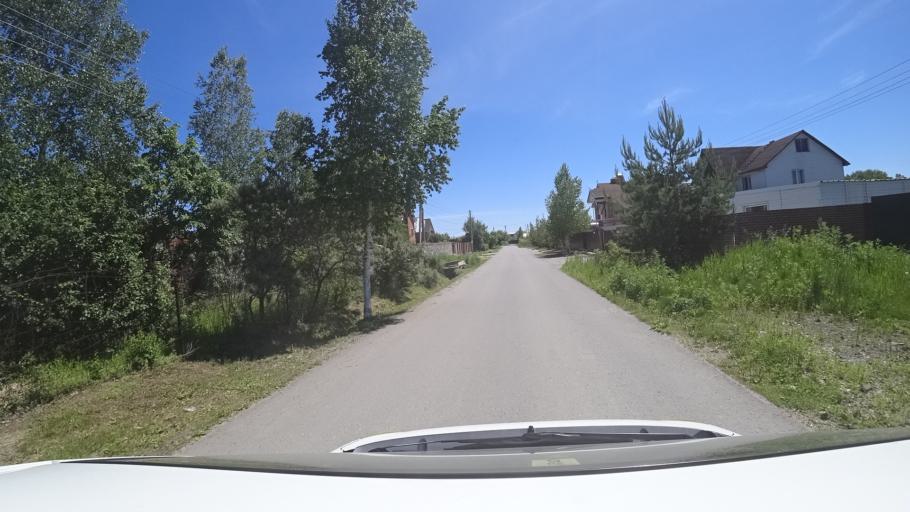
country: RU
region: Khabarovsk Krai
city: Topolevo
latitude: 48.4987
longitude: 135.1813
